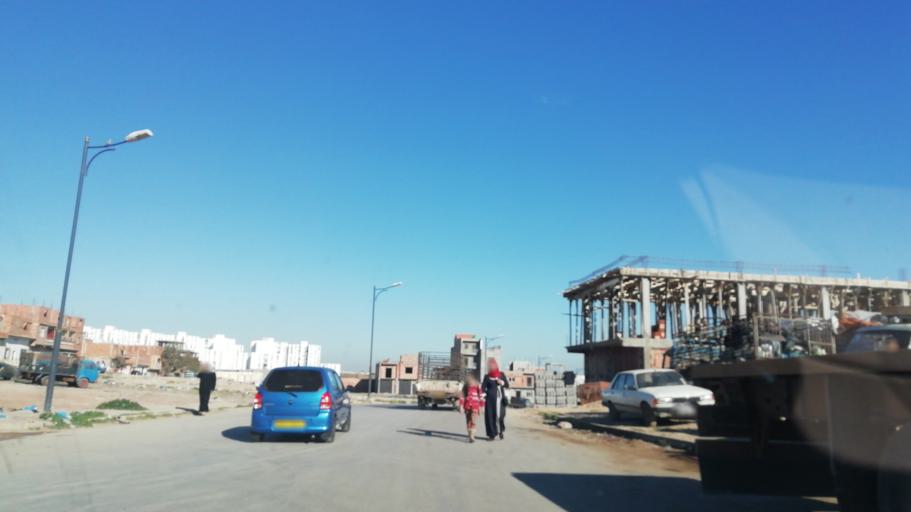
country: DZ
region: Oran
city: Bir el Djir
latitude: 35.7246
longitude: -0.5295
